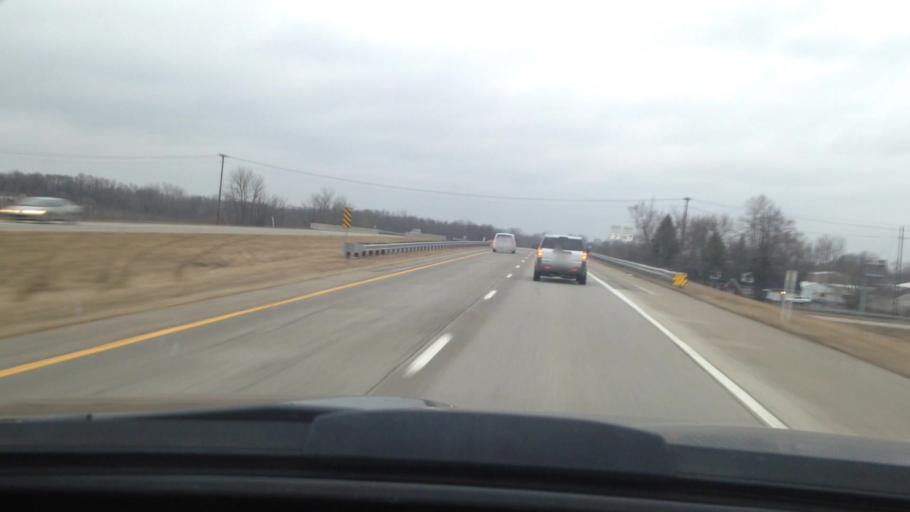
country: US
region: Indiana
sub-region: Delaware County
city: Muncie
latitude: 40.1617
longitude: -85.3535
